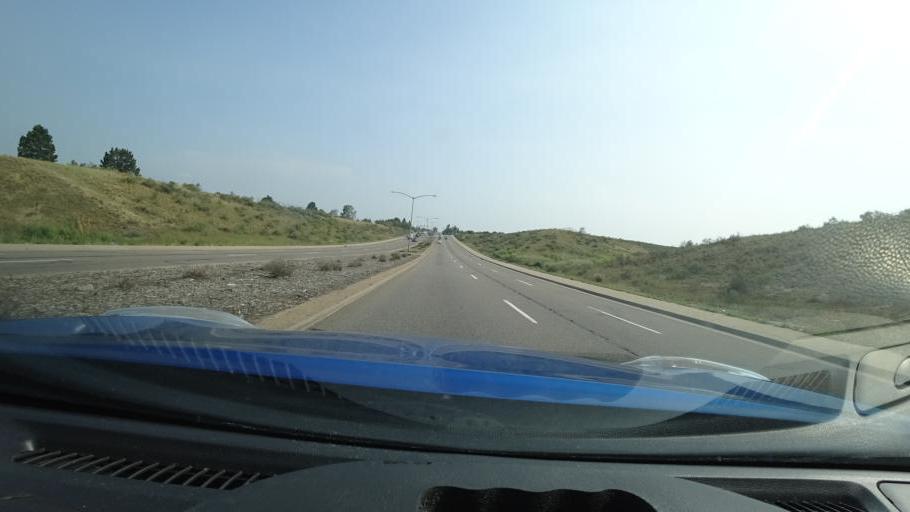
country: US
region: Colorado
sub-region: Adams County
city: Aurora
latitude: 39.6691
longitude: -104.8100
